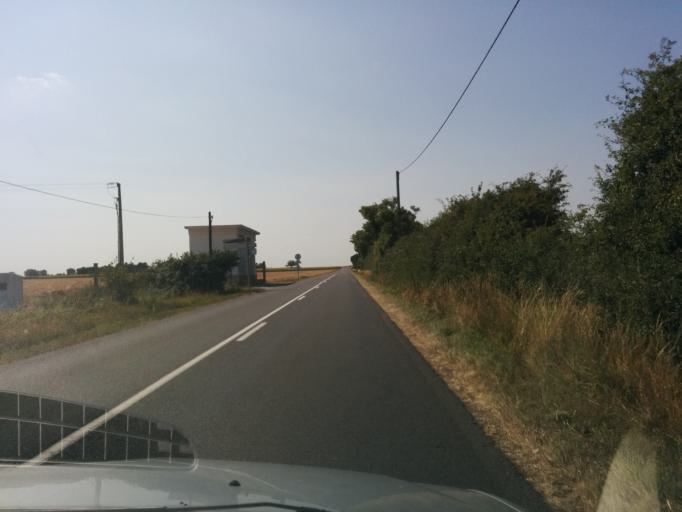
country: FR
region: Poitou-Charentes
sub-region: Departement de la Vienne
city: Saint-Jean-de-Sauves
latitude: 46.7951
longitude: 0.1109
